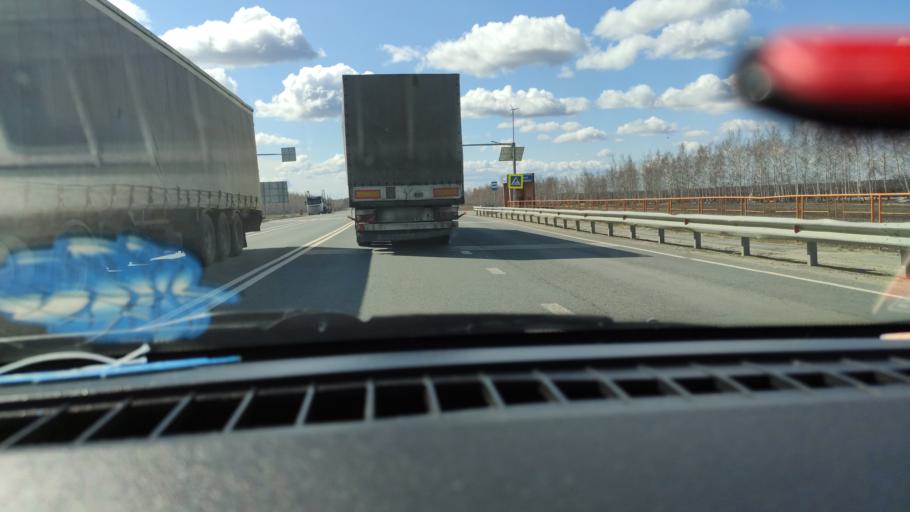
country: RU
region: Samara
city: Syzran'
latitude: 52.9186
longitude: 48.3019
